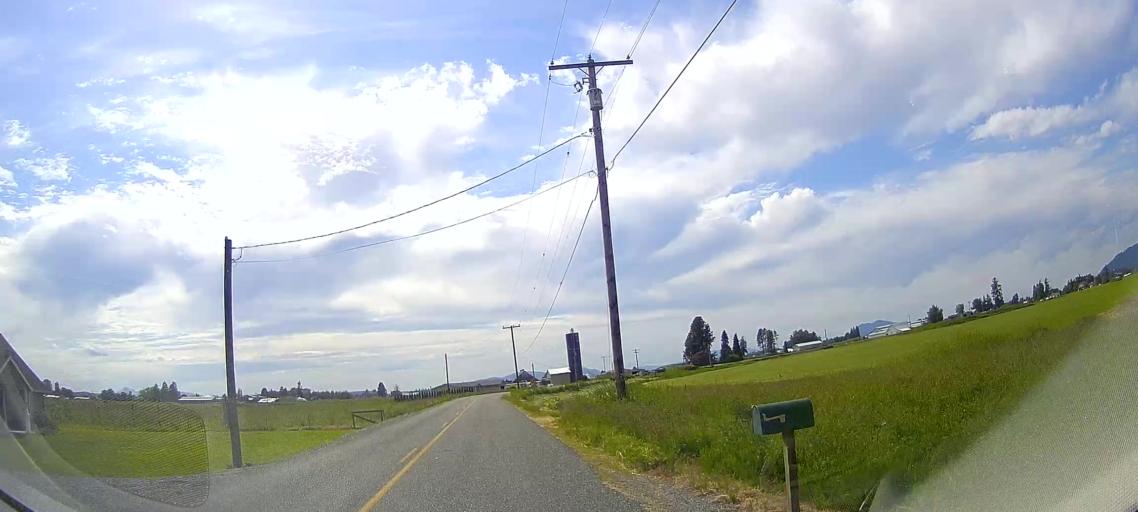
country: US
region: Washington
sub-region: Skagit County
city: Burlington
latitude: 48.5357
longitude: -122.3843
